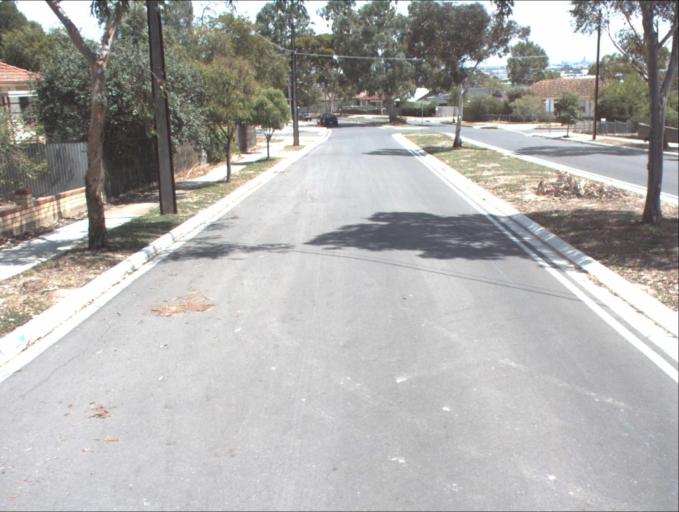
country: AU
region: South Australia
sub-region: Port Adelaide Enfield
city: Enfield
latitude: -34.8505
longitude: 138.6136
